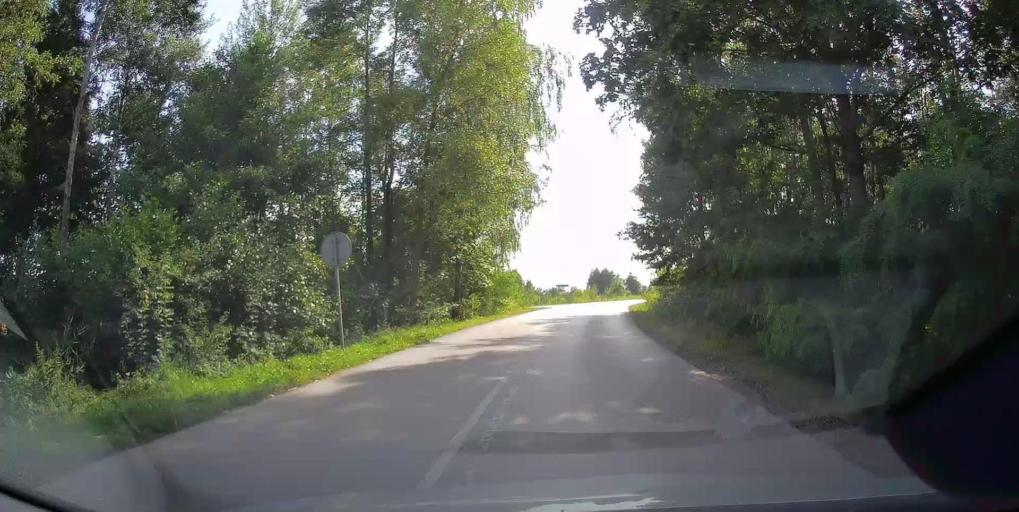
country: PL
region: Lodz Voivodeship
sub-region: Powiat opoczynski
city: Mniszkow
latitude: 51.3378
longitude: 20.0381
